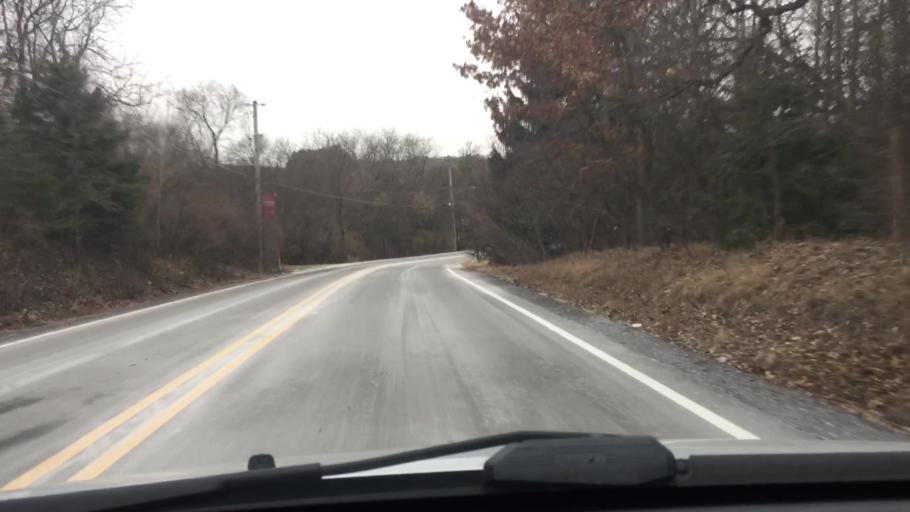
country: US
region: Wisconsin
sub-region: Waukesha County
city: Wales
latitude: 43.0033
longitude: -88.3715
